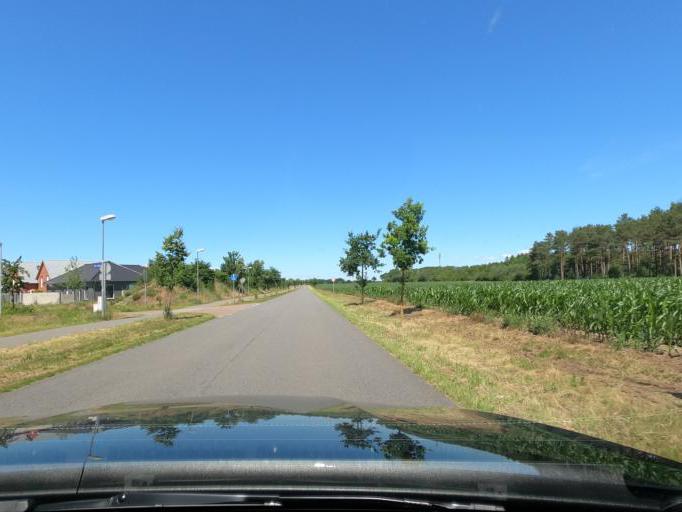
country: DE
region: Lower Saxony
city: Lachendorf
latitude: 52.6142
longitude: 10.2567
